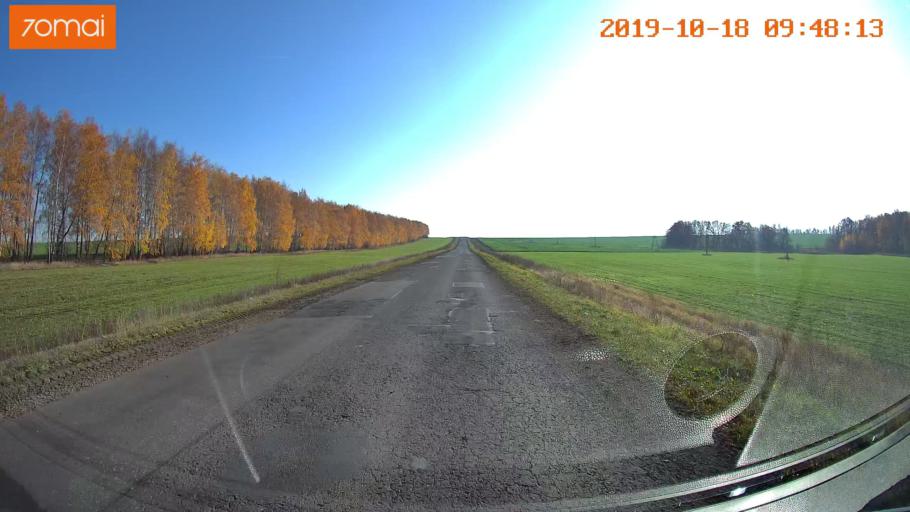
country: RU
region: Tula
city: Kazachka
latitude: 53.3189
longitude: 38.2444
